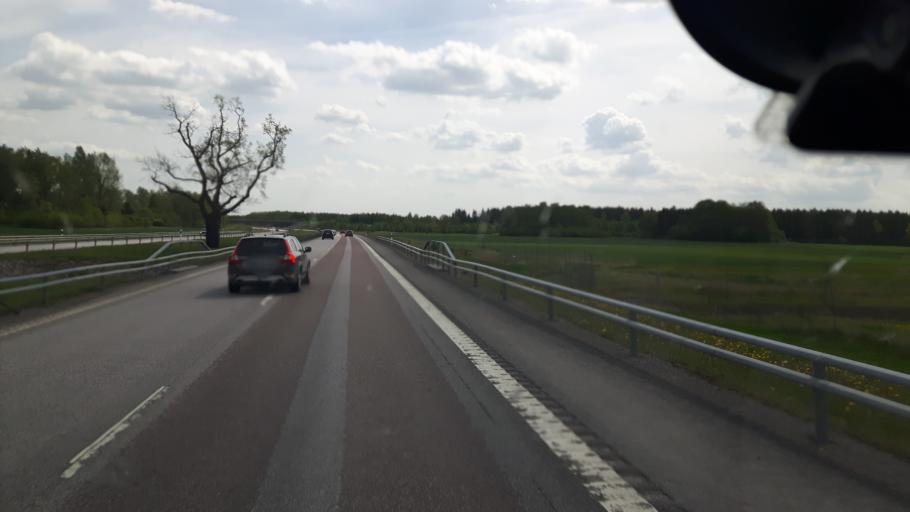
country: SE
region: Uppsala
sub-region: Osthammars Kommun
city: Bjorklinge
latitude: 60.0606
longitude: 17.6130
